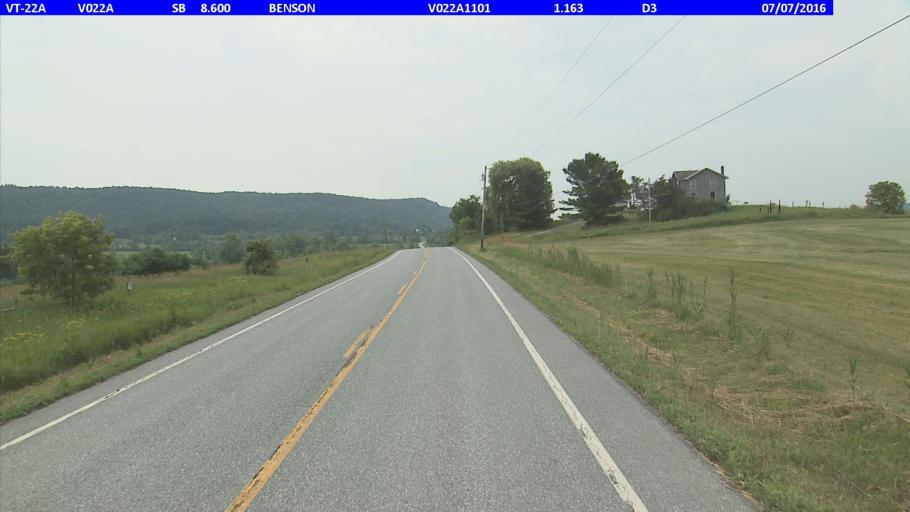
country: US
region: Vermont
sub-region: Rutland County
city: Fair Haven
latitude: 43.6860
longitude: -73.2899
